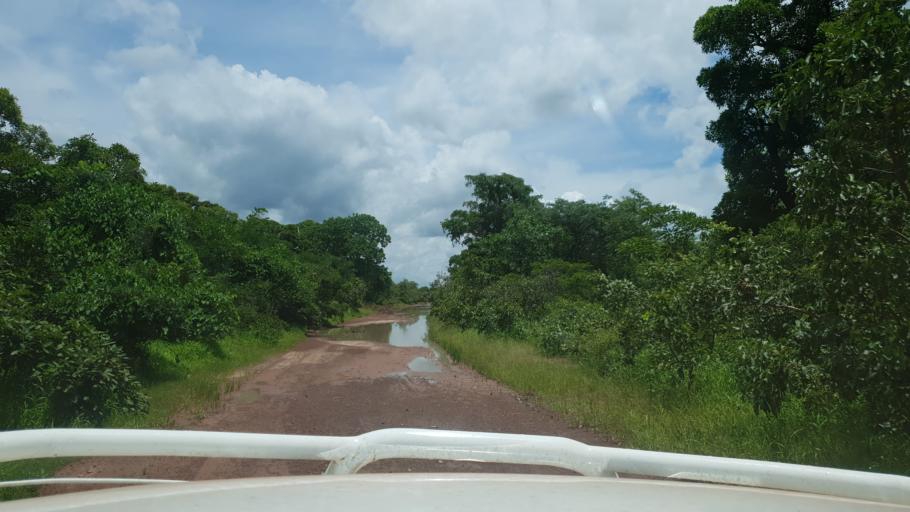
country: ML
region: Koulikoro
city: Banamba
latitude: 13.2007
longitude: -7.3340
